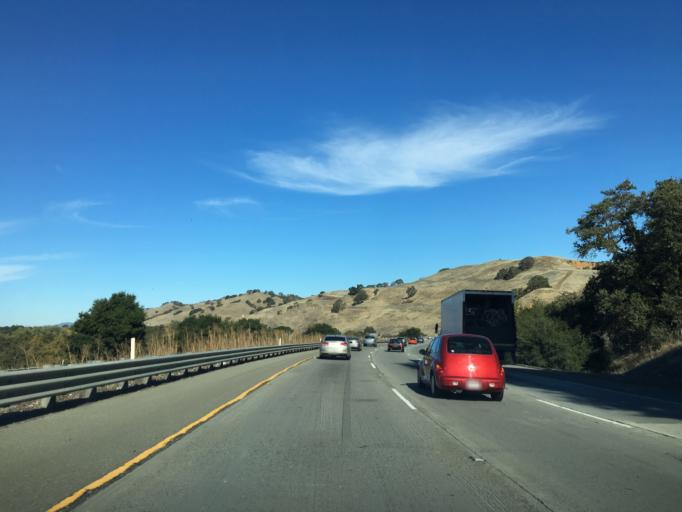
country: US
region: California
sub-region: Alameda County
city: Pleasanton
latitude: 37.5986
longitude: -121.8734
